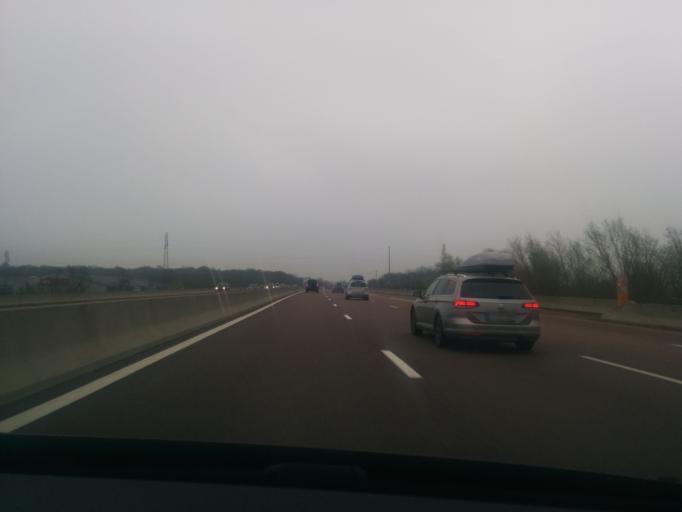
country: FR
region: Bourgogne
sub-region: Departement de la Cote-d'Or
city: Chevigny-Saint-Sauveur
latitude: 47.2858
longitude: 5.1566
